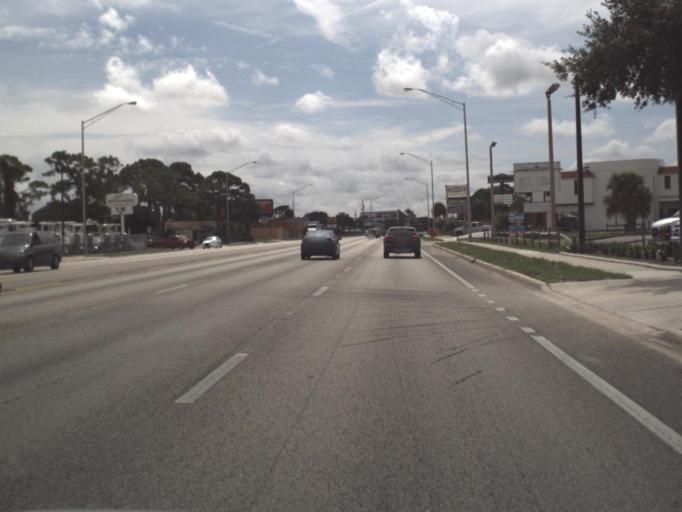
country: US
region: Florida
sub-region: Manatee County
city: Whitfield
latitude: 27.4011
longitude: -82.5655
